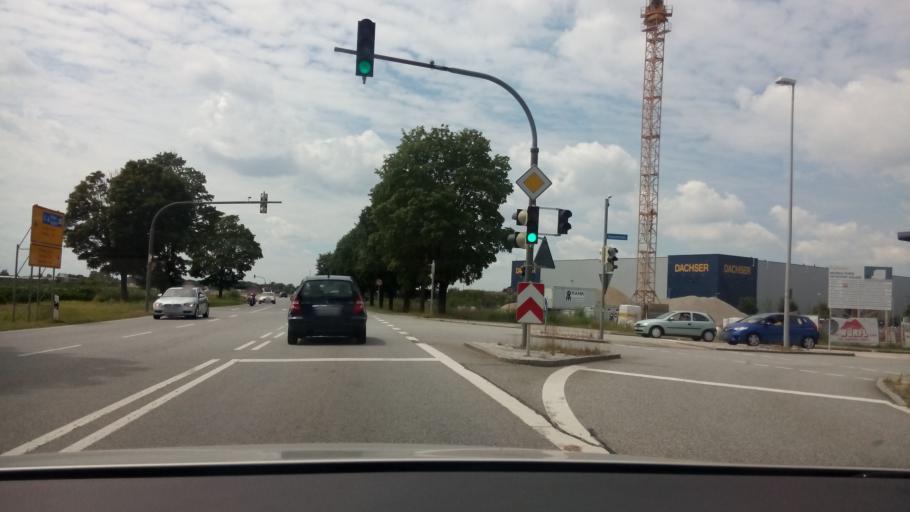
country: DE
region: Bavaria
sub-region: Upper Bavaria
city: Neufahrn bei Freising
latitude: 48.3298
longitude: 11.6950
